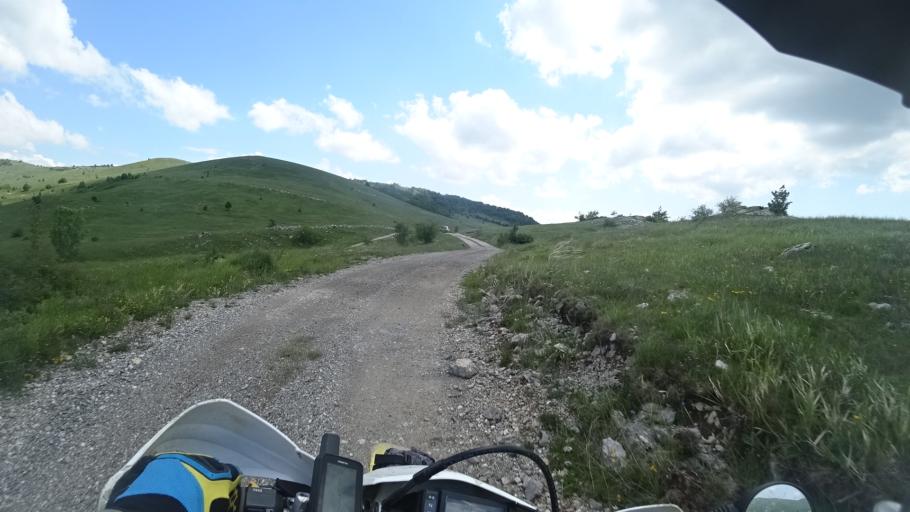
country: HR
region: Zadarska
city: Gracac
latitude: 44.2993
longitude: 15.9458
